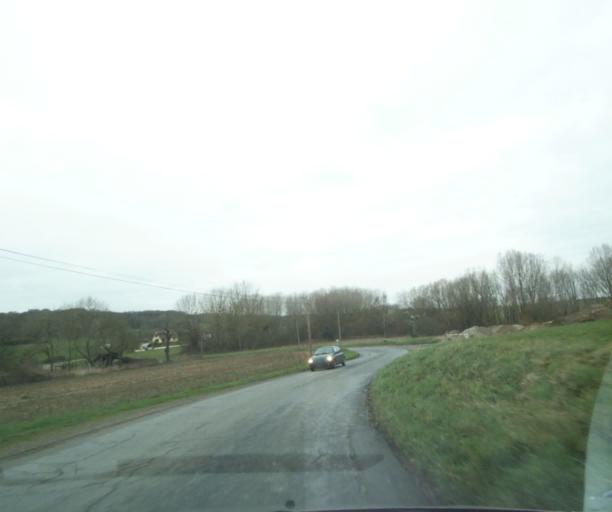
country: FR
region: Picardie
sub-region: Departement de l'Oise
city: Noyon
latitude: 49.5808
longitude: 2.9703
